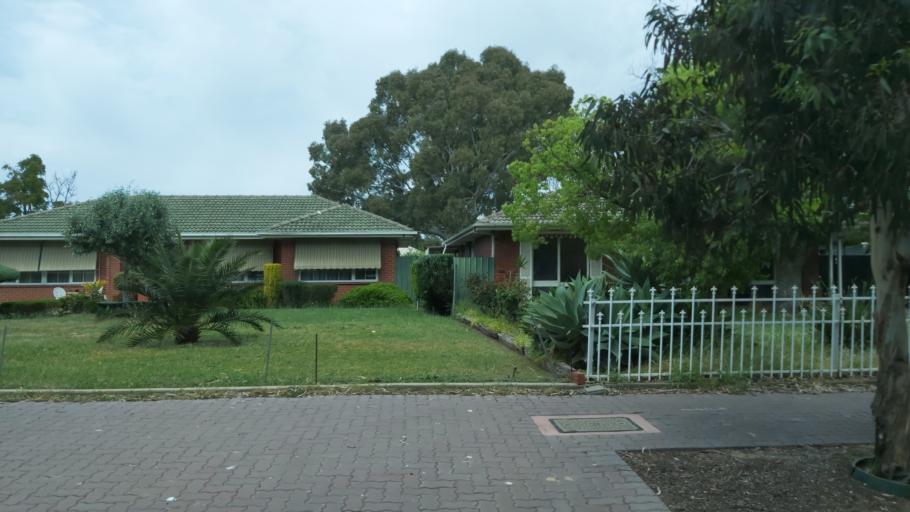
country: AU
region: South Australia
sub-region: Marion
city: Clovelly Park
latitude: -34.9926
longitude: 138.5826
